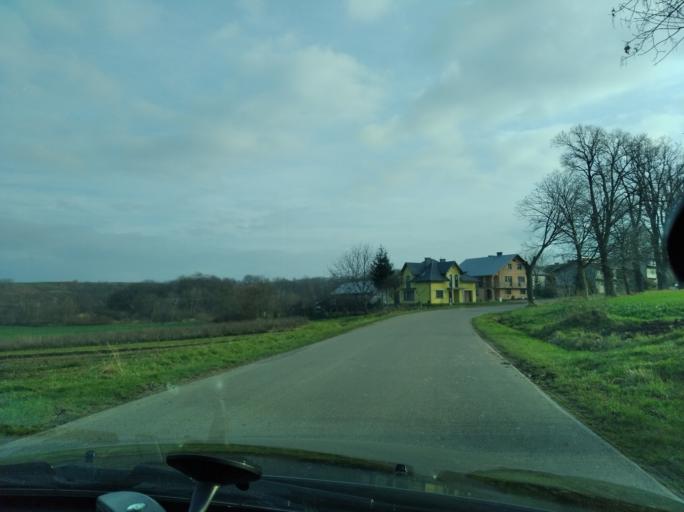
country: PL
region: Subcarpathian Voivodeship
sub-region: Powiat przeworski
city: Lopuszka Wielka
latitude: 49.9531
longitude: 22.4080
